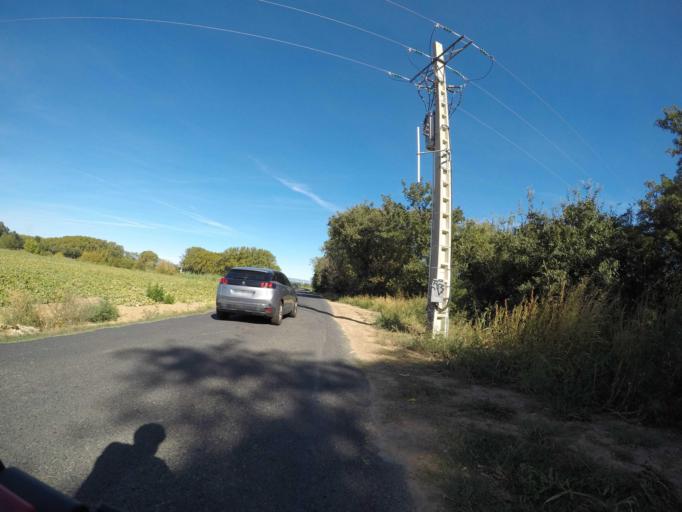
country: FR
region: Languedoc-Roussillon
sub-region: Departement des Pyrenees-Orientales
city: Le Soler
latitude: 42.6603
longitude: 2.7965
